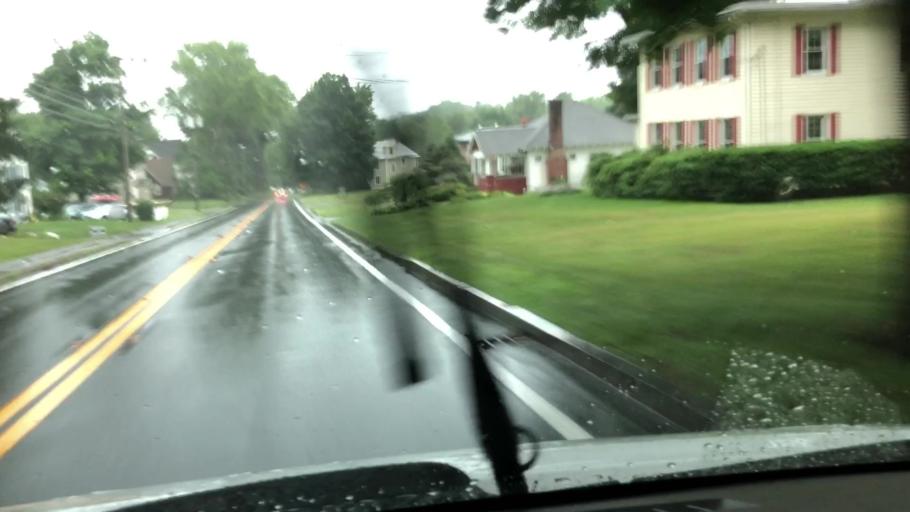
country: US
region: Massachusetts
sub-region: Berkshire County
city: Lee
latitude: 42.3143
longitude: -73.2559
